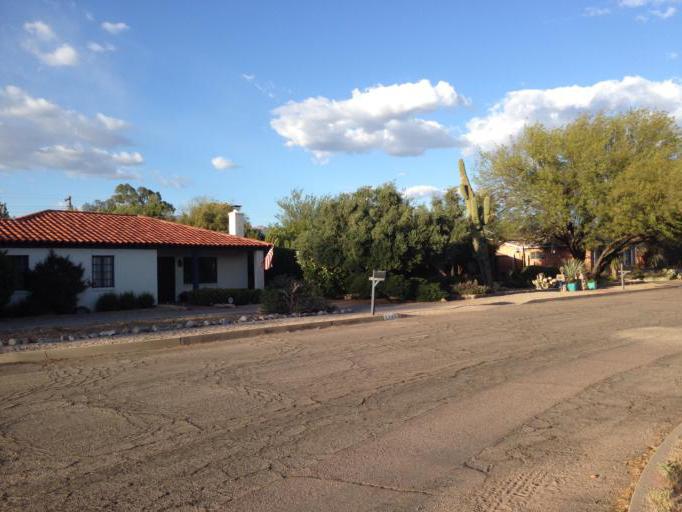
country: US
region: Arizona
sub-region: Pima County
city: Tucson
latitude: 32.2474
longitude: -110.9384
